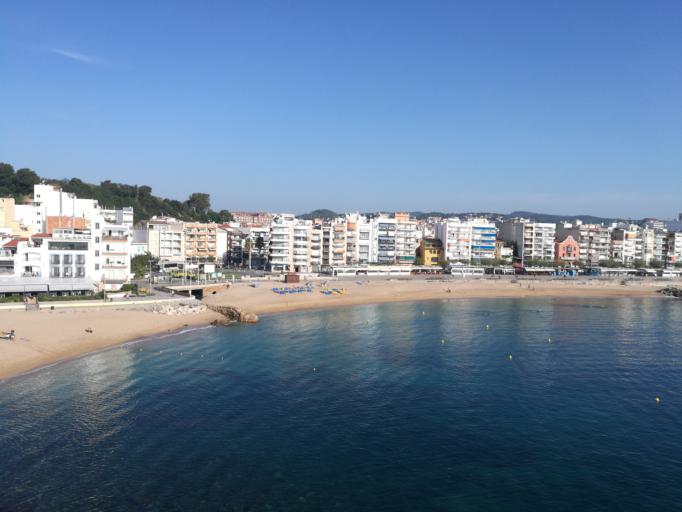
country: ES
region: Catalonia
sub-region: Provincia de Girona
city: Blanes
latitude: 41.6707
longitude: 2.7919
